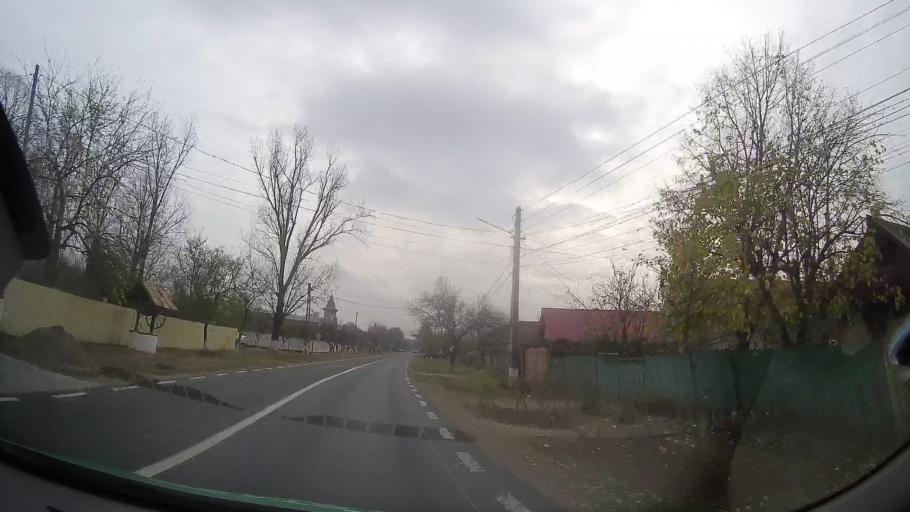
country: RO
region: Ilfov
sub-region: Comuna Gruiu
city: Lipia
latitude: 44.7165
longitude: 26.2737
